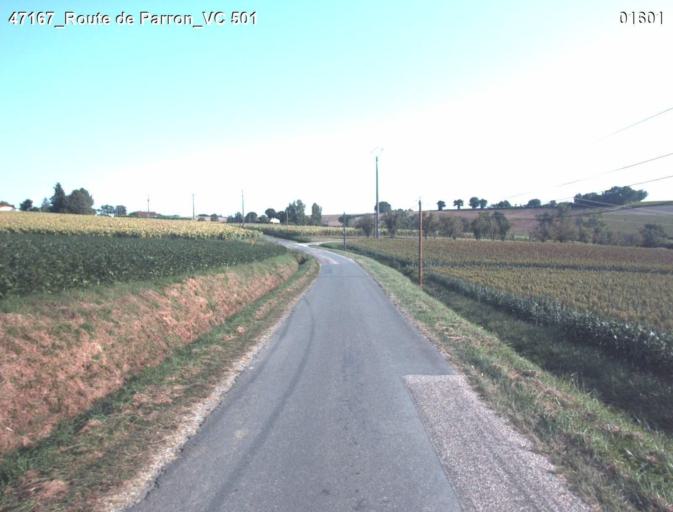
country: FR
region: Aquitaine
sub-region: Departement du Lot-et-Garonne
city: Mezin
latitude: 44.0490
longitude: 0.2635
